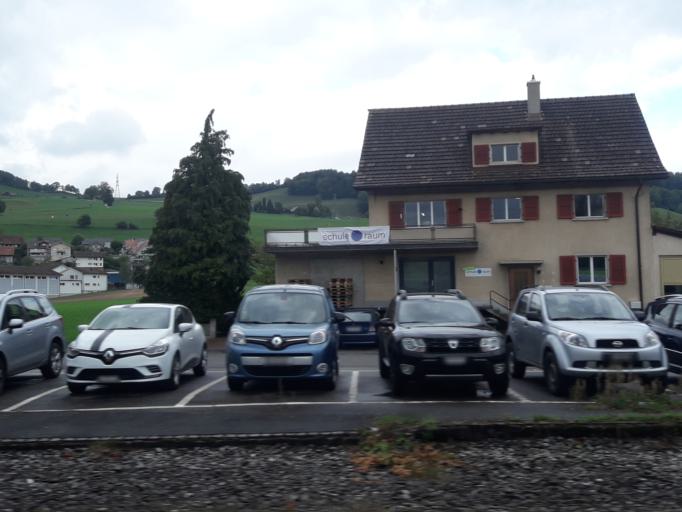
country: CH
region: Bern
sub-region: Bern-Mittelland District
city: Muhlethurnen
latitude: 46.8130
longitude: 7.5140
